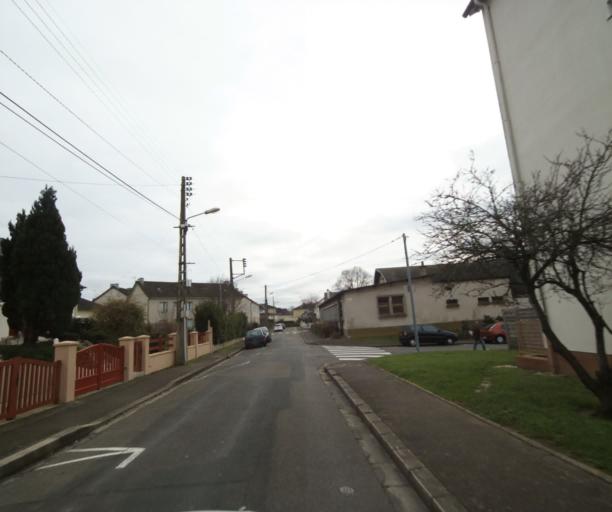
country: FR
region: Pays de la Loire
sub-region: Departement de la Sarthe
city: Le Mans
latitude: 47.9743
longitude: 0.2028
